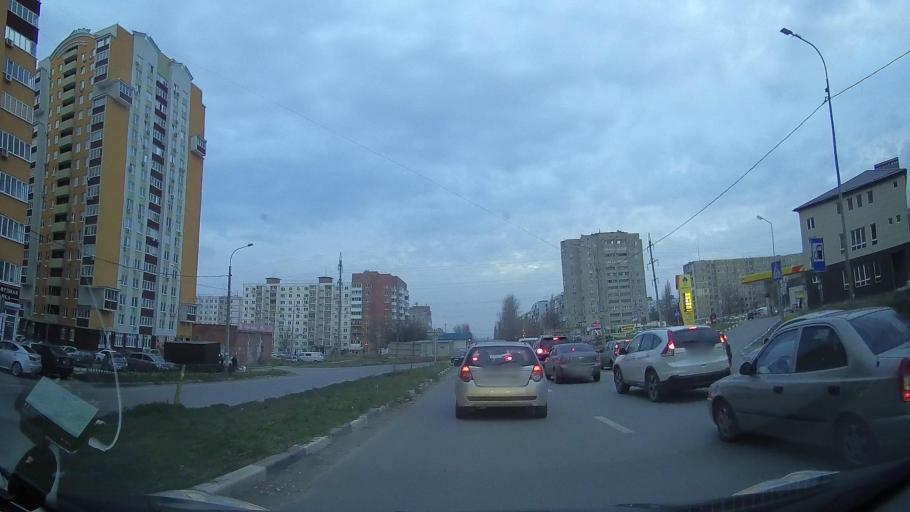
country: RU
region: Rostov
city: Severnyy
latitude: 47.3032
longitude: 39.7226
